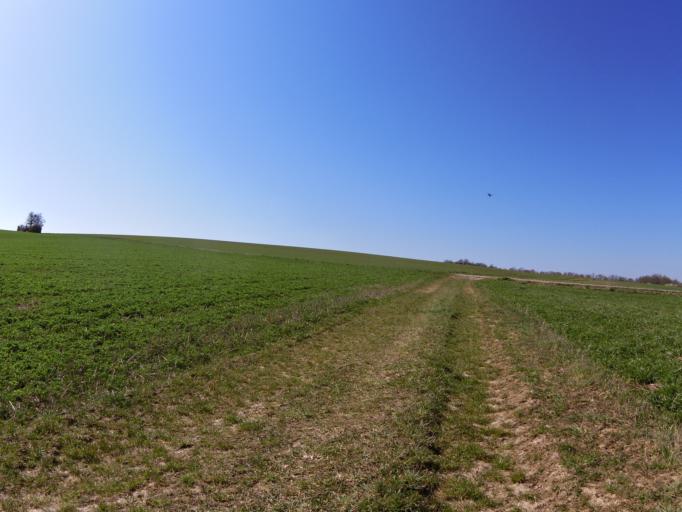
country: DE
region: Bavaria
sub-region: Regierungsbezirk Unterfranken
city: Kurnach
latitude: 49.8392
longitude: 10.0353
